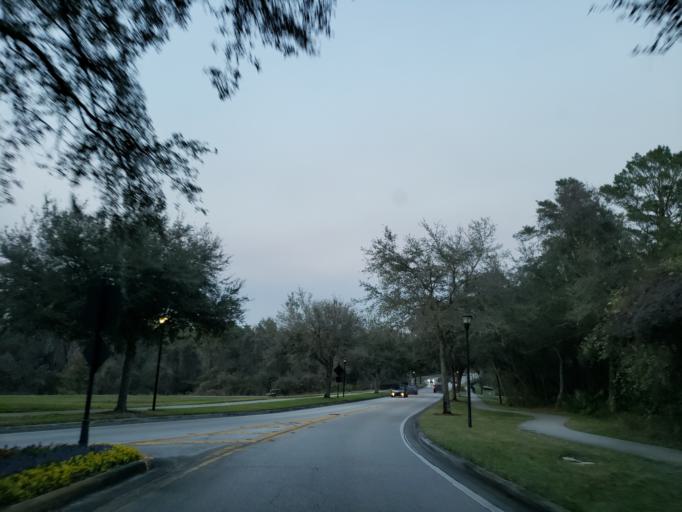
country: US
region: Florida
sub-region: Hillsborough County
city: Fish Hawk
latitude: 27.8495
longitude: -82.2090
